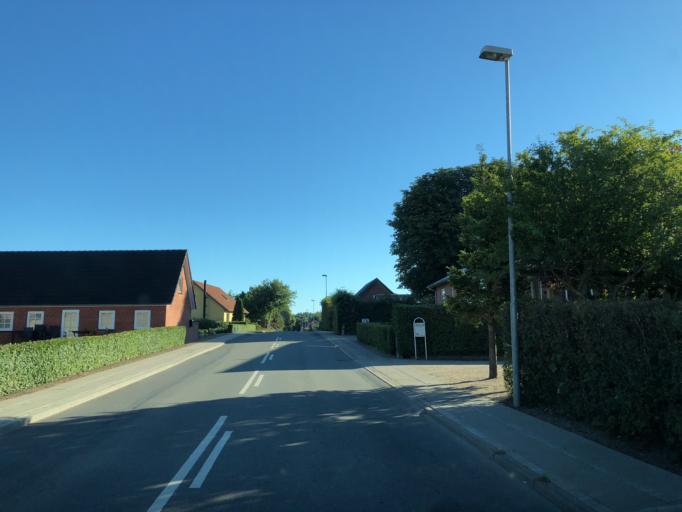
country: DK
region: Central Jutland
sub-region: Viborg Kommune
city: Stoholm
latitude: 56.4722
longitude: 9.2271
